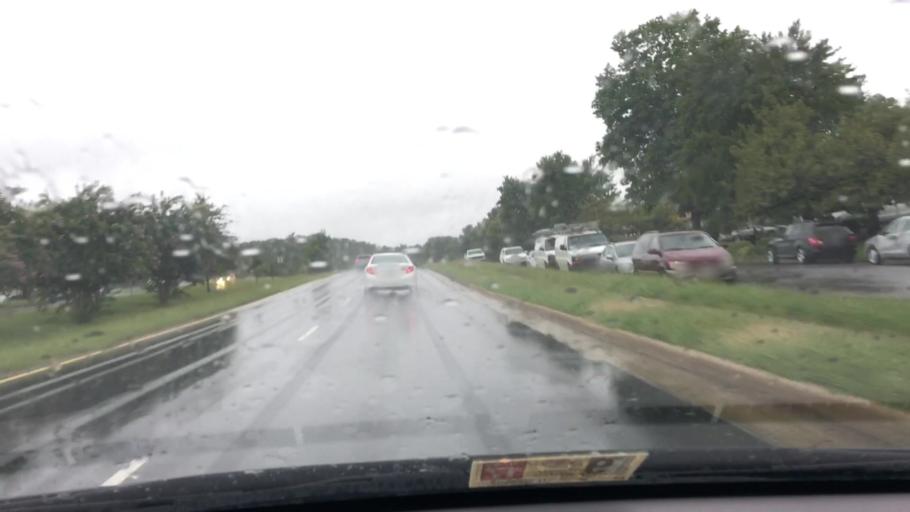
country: US
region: Virginia
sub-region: Loudoun County
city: Oak Grove
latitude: 39.0104
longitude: -77.3950
